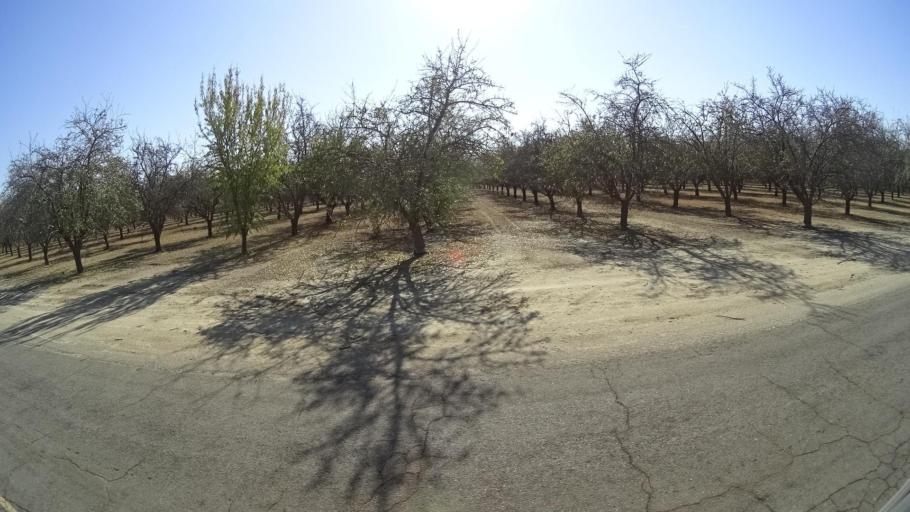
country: US
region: California
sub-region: Kern County
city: McFarland
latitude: 35.7035
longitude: -119.1452
